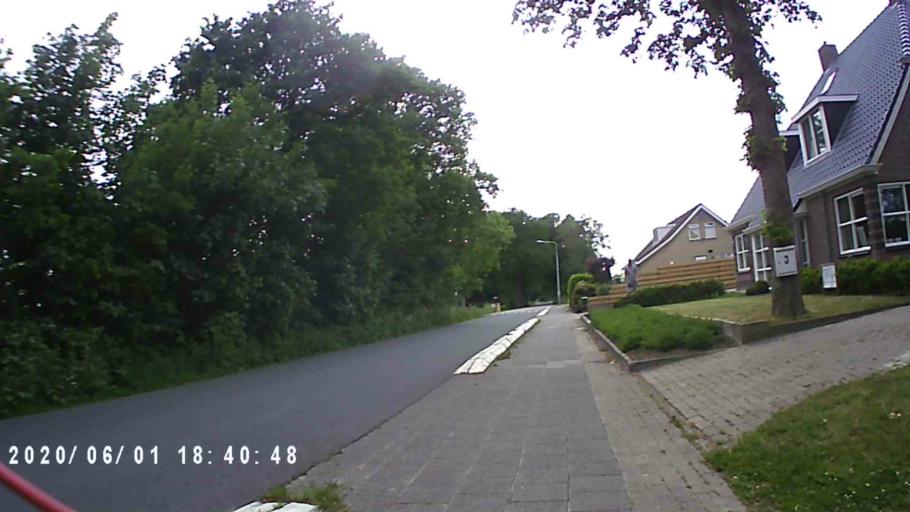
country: NL
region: Friesland
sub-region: Gemeente Tytsjerksteradiel
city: Eastermar
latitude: 53.1736
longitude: 6.0665
